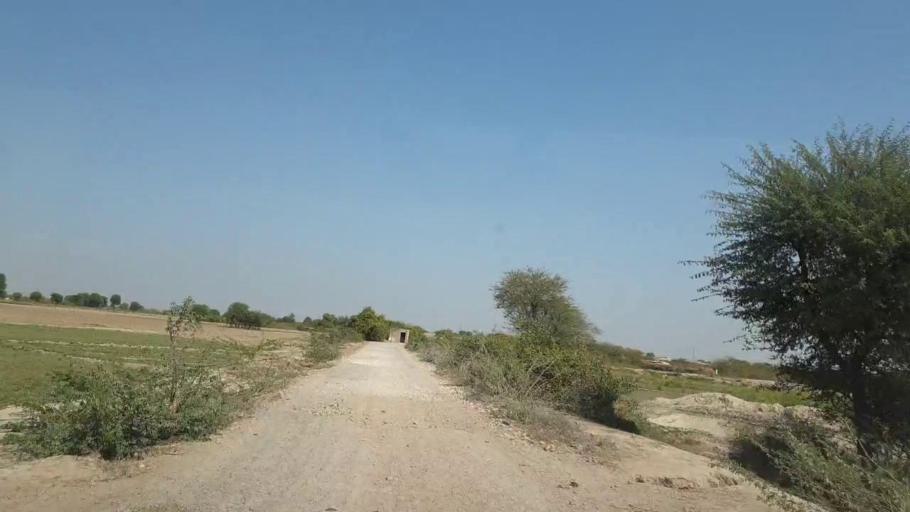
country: PK
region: Sindh
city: Kunri
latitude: 25.0919
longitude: 69.5265
